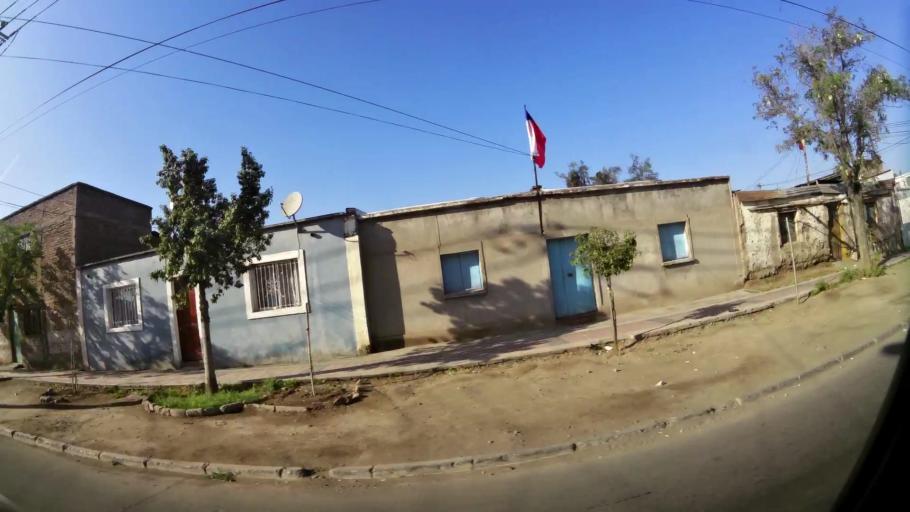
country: CL
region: Santiago Metropolitan
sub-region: Provincia de Santiago
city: Santiago
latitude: -33.4903
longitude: -70.6307
